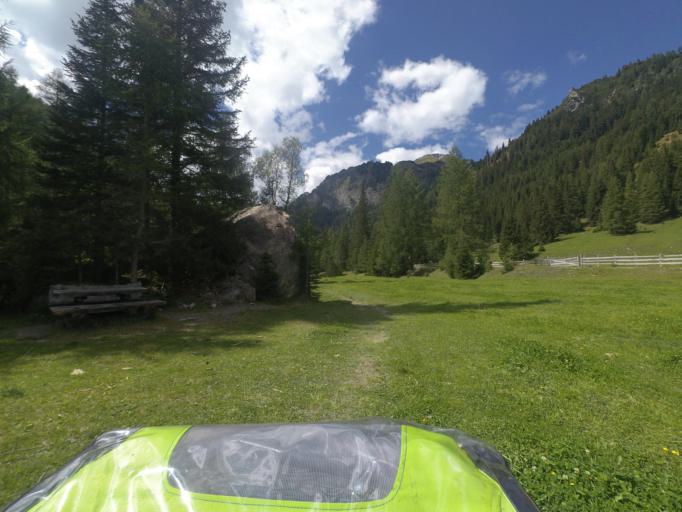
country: AT
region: Salzburg
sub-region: Politischer Bezirk Sankt Johann im Pongau
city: Kleinarl
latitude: 47.1873
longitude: 13.3765
